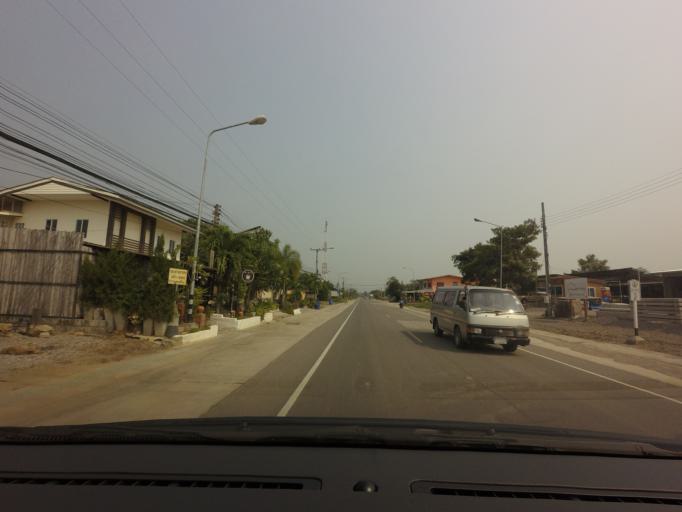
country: TH
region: Prachuap Khiri Khan
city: Kui Buri
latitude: 12.0666
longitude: 99.8774
